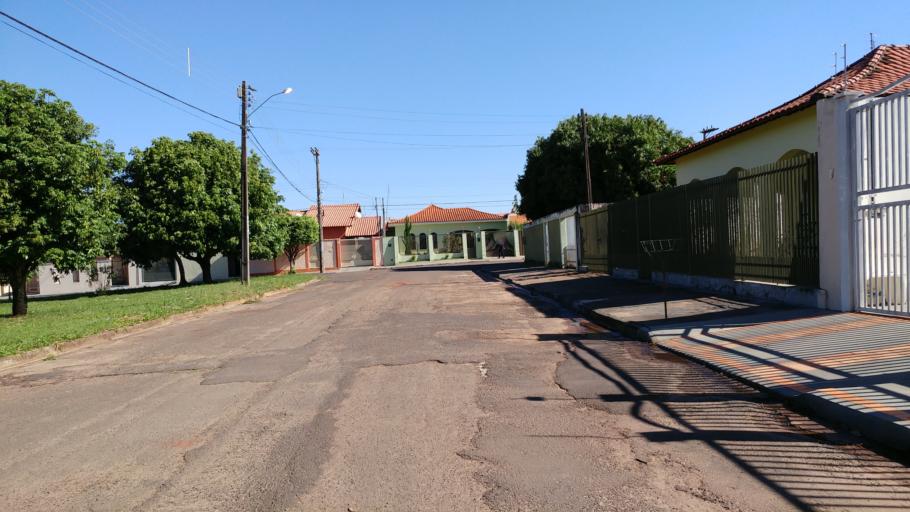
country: BR
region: Sao Paulo
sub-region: Paraguacu Paulista
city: Paraguacu Paulista
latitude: -22.4041
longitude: -50.5785
